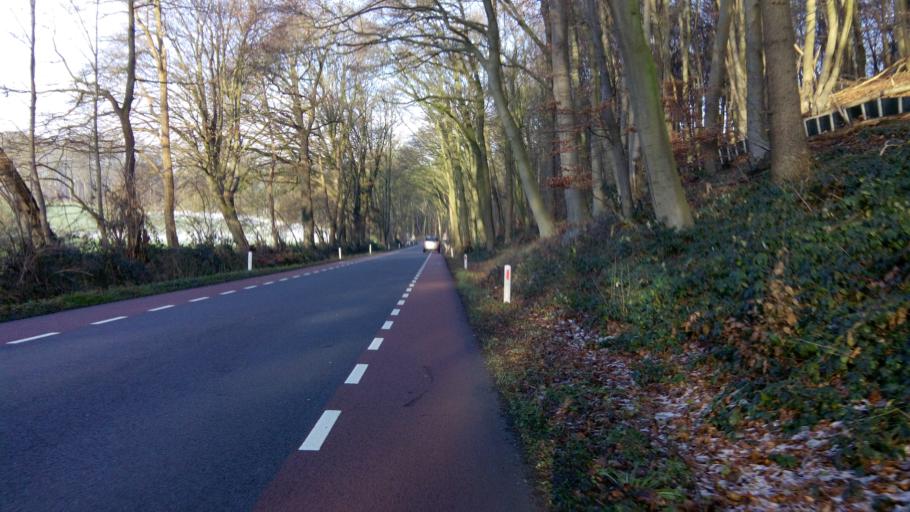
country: NL
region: Gelderland
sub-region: Gemeente Groesbeek
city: Berg en Dal
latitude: 51.8118
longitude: 5.9469
